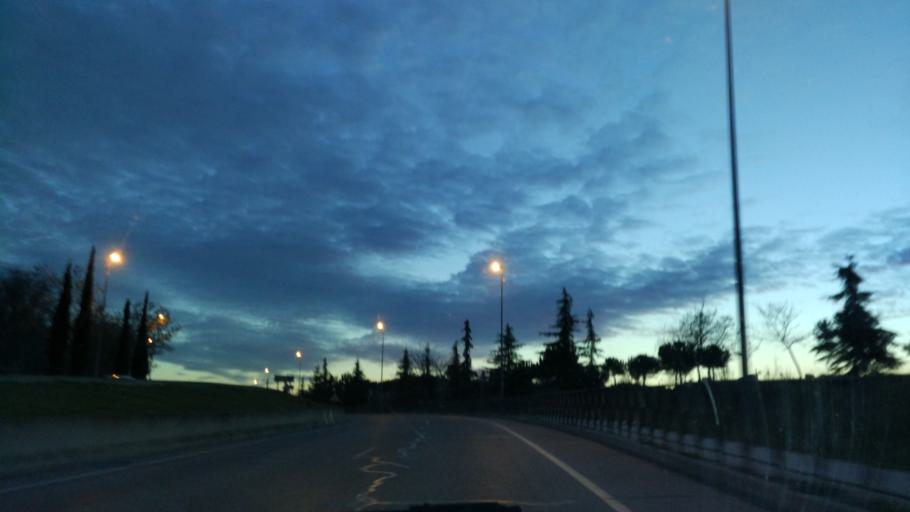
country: ES
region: Madrid
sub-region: Provincia de Madrid
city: Leganes
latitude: 40.3415
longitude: -3.7703
